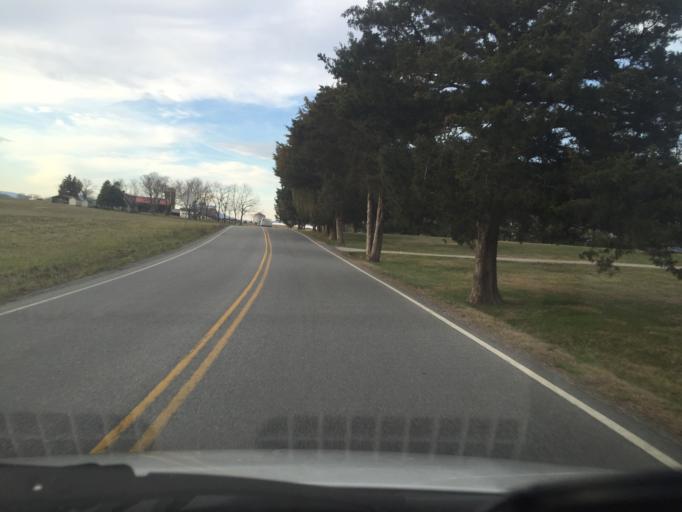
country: US
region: Virginia
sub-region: Bedford County
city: Forest
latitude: 37.3273
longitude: -79.3021
